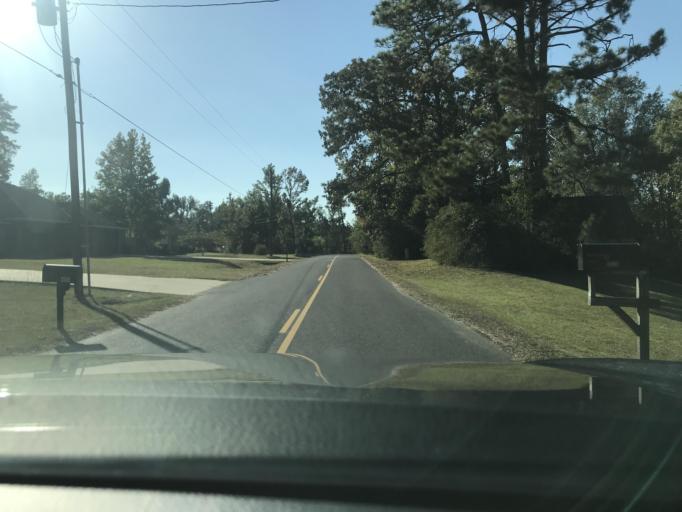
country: US
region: Louisiana
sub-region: Calcasieu Parish
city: Westlake
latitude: 30.3153
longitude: -93.2731
